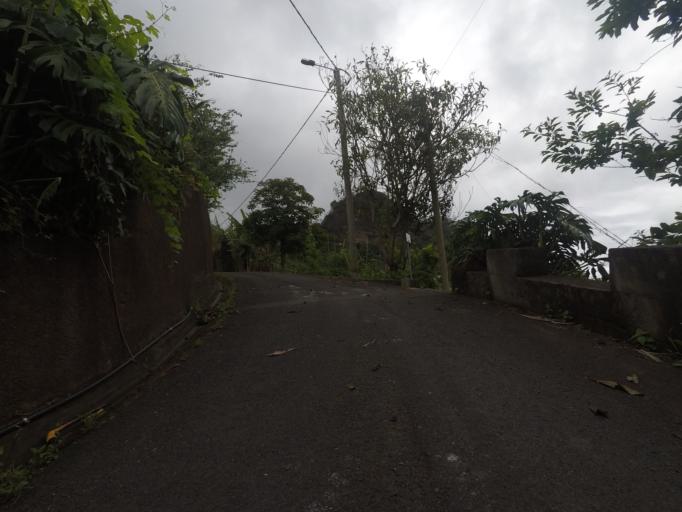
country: PT
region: Madeira
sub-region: Santana
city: Santana
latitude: 32.7563
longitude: -16.8778
